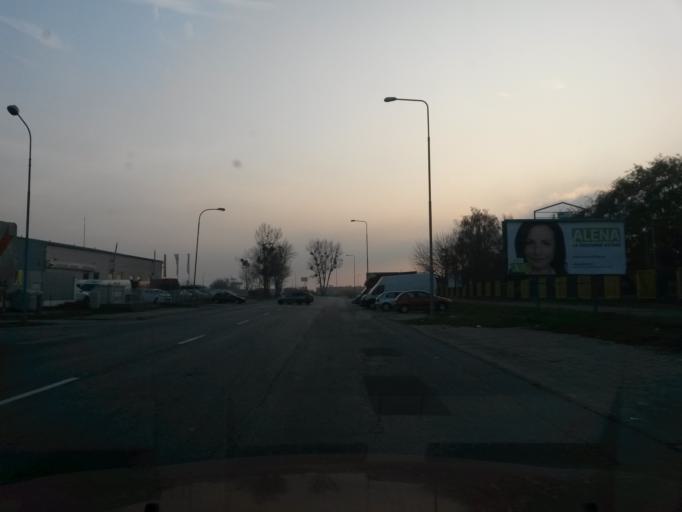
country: SK
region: Kosicky
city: Kosice
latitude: 48.6999
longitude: 21.2492
